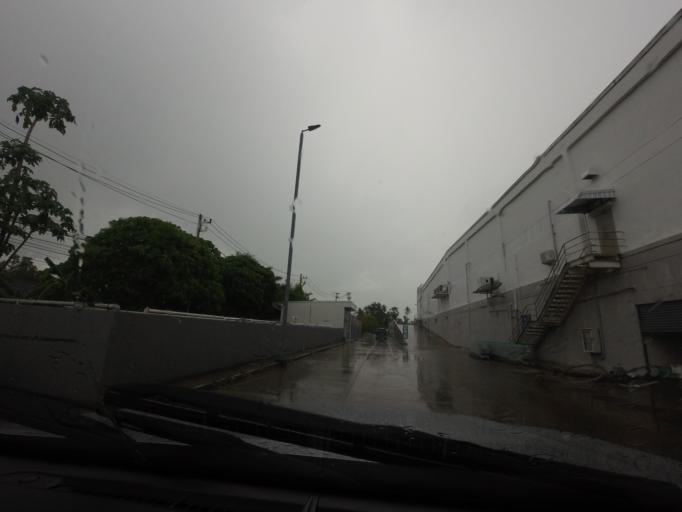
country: TH
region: Chumphon
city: Chumphon
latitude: 10.5035
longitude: 99.1380
